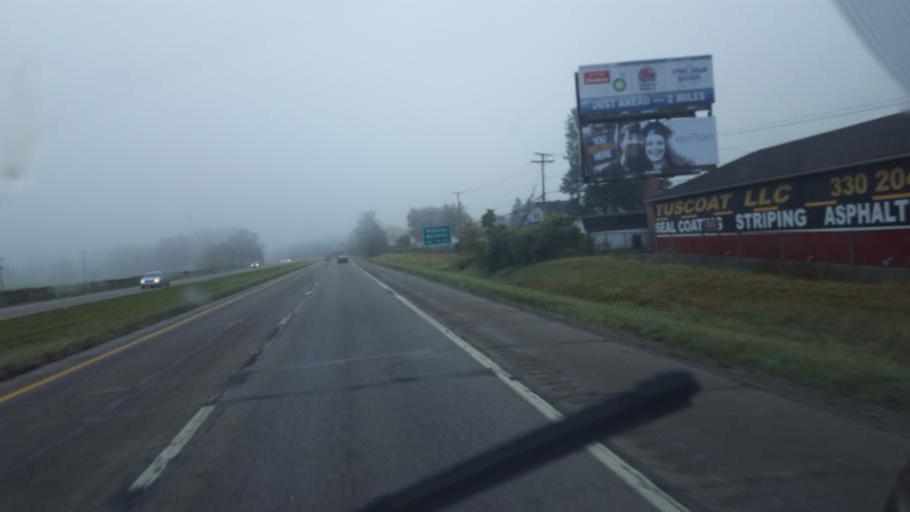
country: US
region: Ohio
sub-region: Tuscarawas County
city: Tuscarawas
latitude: 40.4443
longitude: -81.3878
